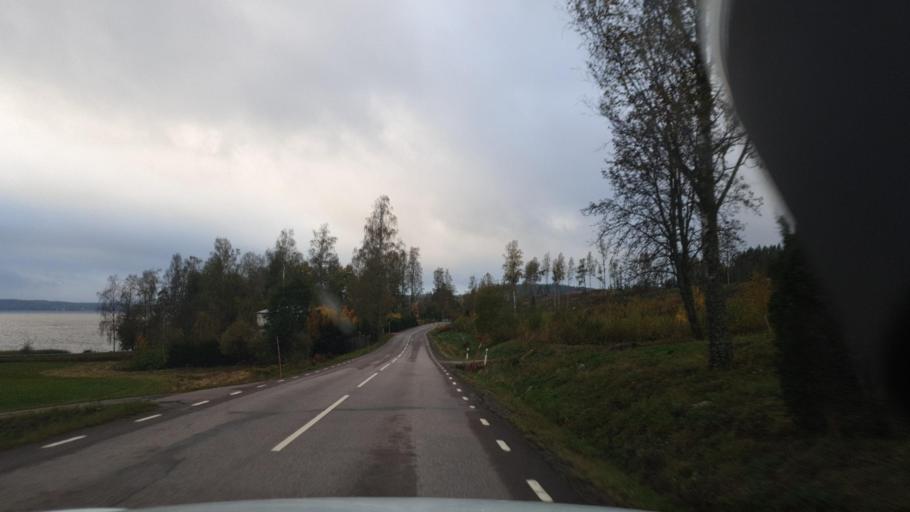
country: SE
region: Vaermland
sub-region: Arvika Kommun
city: Arvika
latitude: 59.7303
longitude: 12.6428
